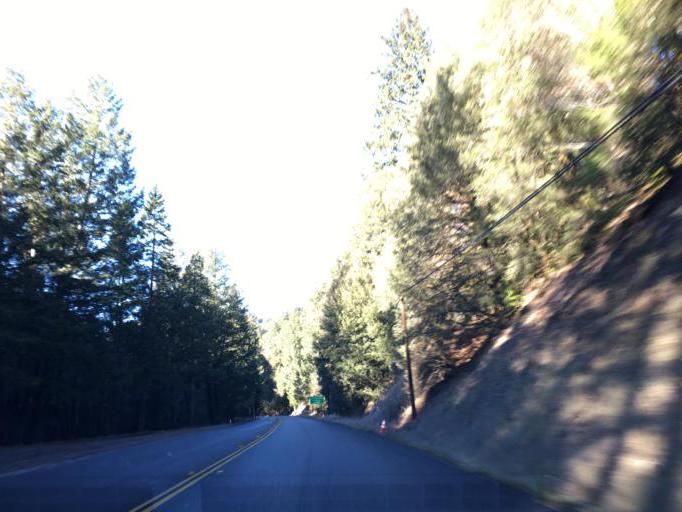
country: US
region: California
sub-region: Mendocino County
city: Laytonville
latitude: 39.8011
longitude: -123.5432
